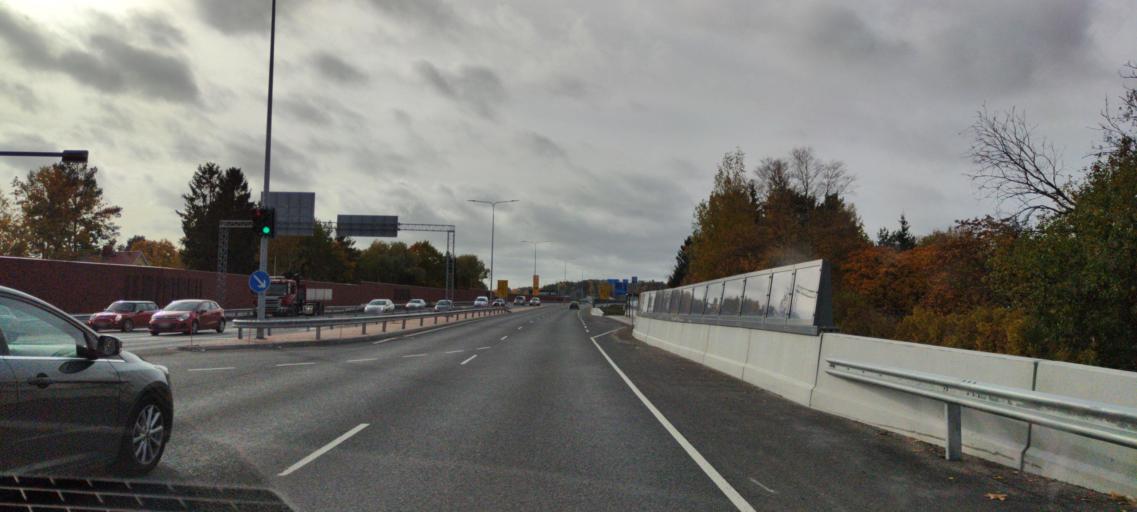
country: FI
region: Varsinais-Suomi
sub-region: Turku
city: Kaarina
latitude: 60.4690
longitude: 22.3529
